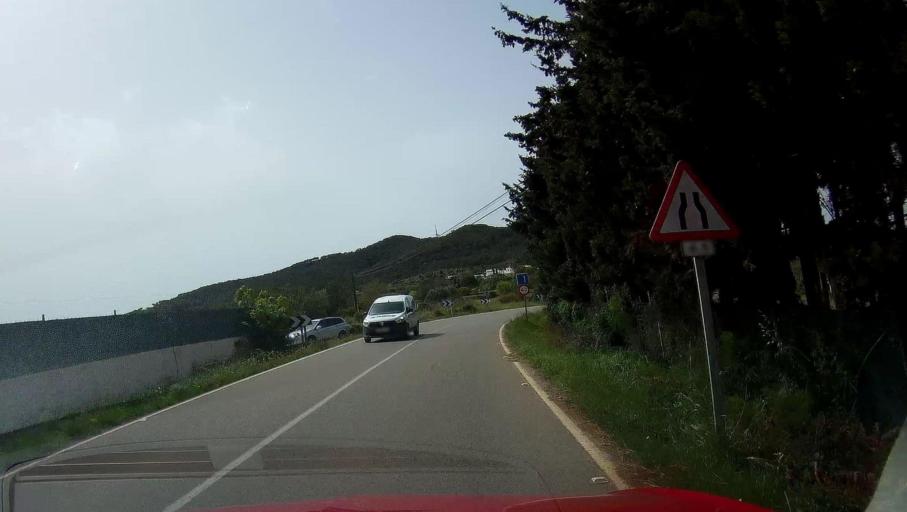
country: ES
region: Balearic Islands
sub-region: Illes Balears
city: Santa Eularia des Riu
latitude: 38.9863
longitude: 1.4910
